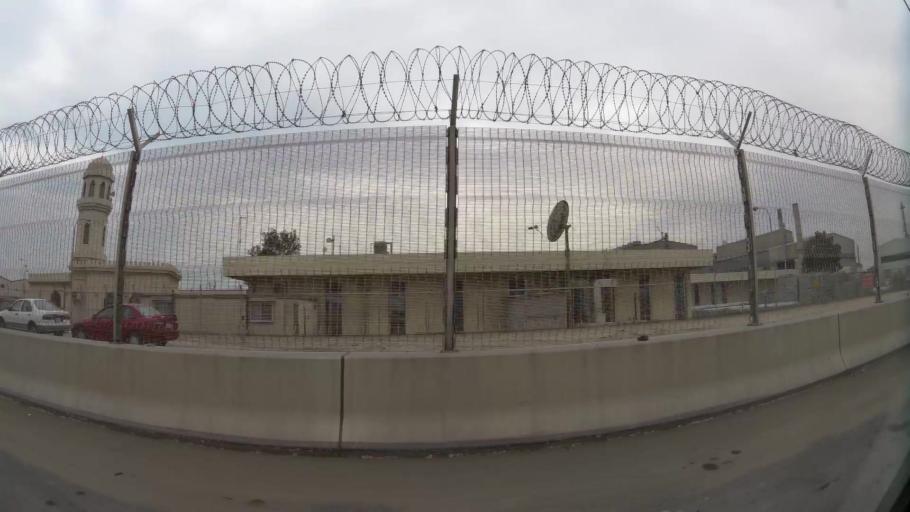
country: BH
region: Northern
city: Sitrah
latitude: 26.1851
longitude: 50.6144
